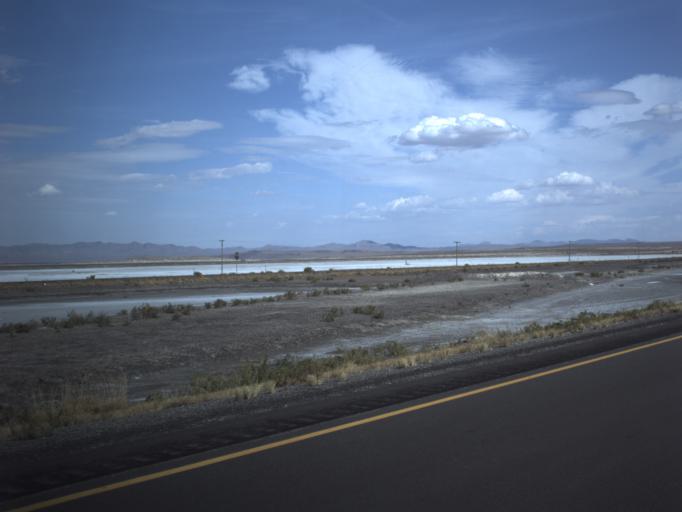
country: US
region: Utah
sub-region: Tooele County
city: Wendover
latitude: 40.7266
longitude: -113.2726
